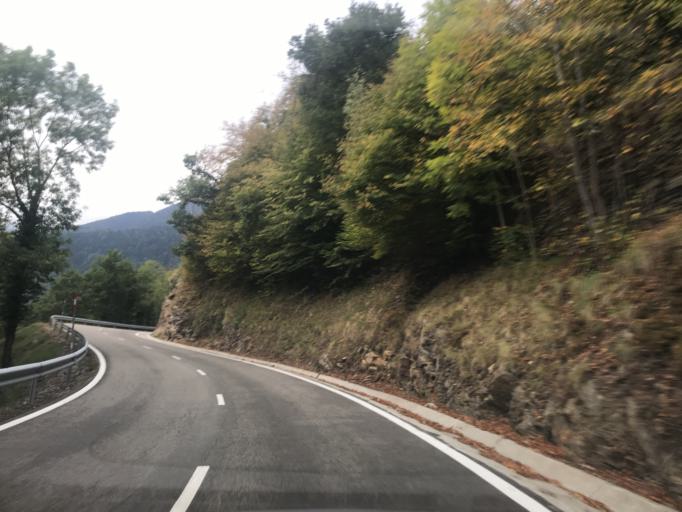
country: ES
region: Catalonia
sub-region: Provincia de Lleida
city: Les
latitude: 42.7780
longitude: 0.6829
